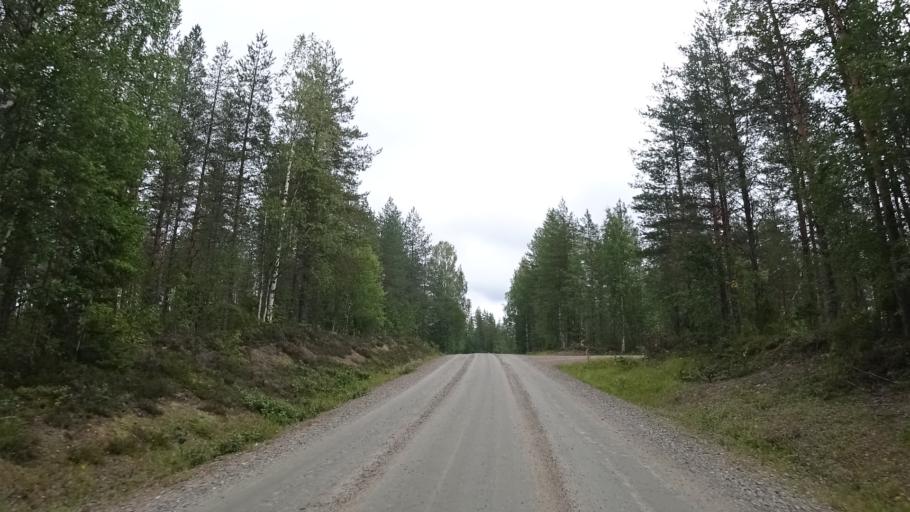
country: FI
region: North Karelia
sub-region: Joensuu
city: Ilomantsi
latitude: 63.0367
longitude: 31.2032
